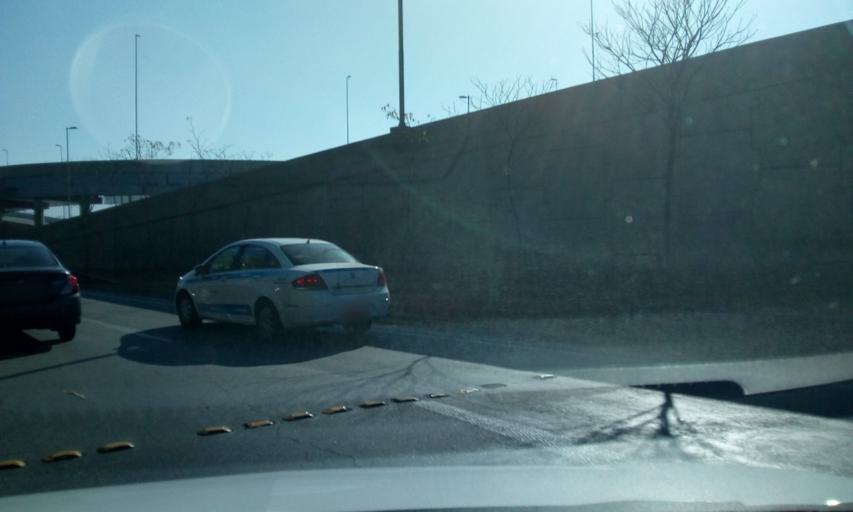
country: BR
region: Sao Paulo
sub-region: Guarulhos
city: Guarulhos
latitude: -23.4251
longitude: -46.4795
